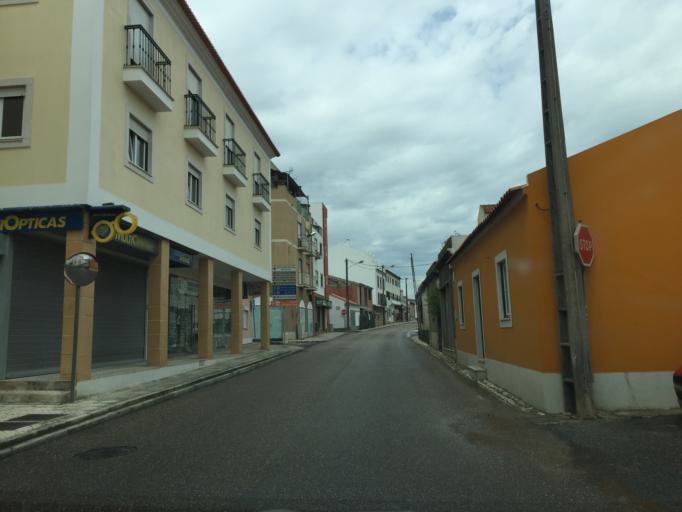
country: PT
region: Lisbon
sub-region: Azambuja
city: Aveiras de Cima
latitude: 39.1384
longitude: -8.8992
